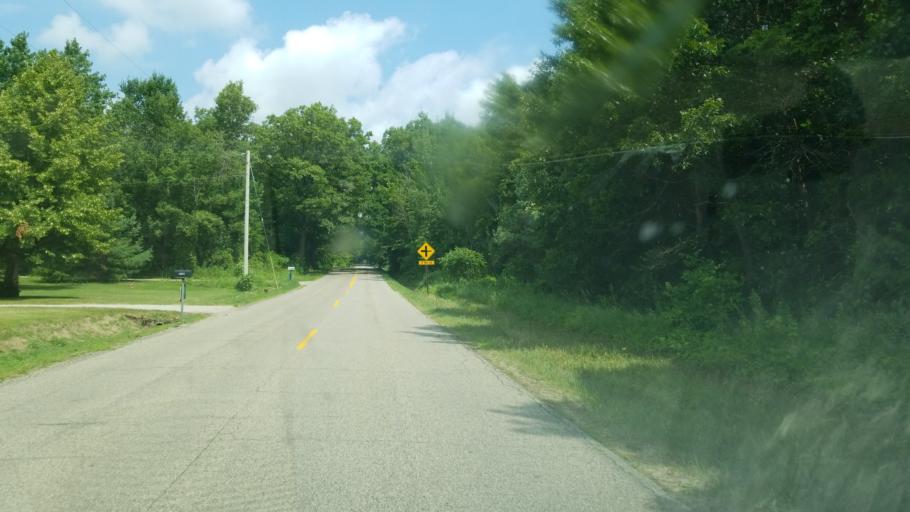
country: US
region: Michigan
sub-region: Kent County
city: Cedar Springs
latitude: 43.2475
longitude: -85.5112
